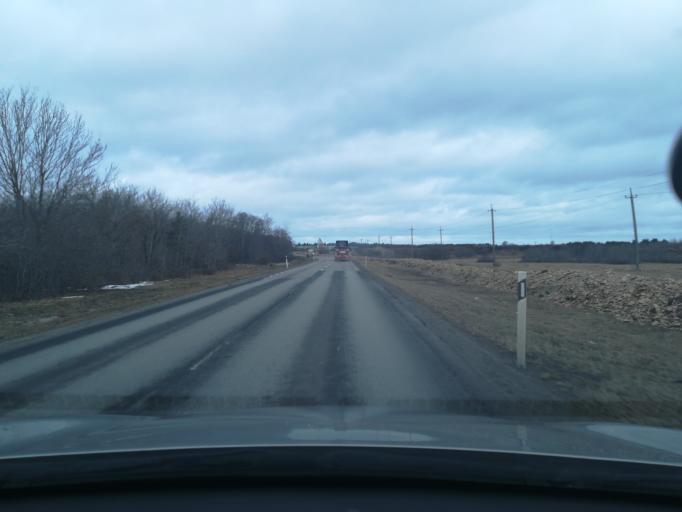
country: EE
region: Harju
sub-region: Harku vald
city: Tabasalu
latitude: 59.3966
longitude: 24.5535
